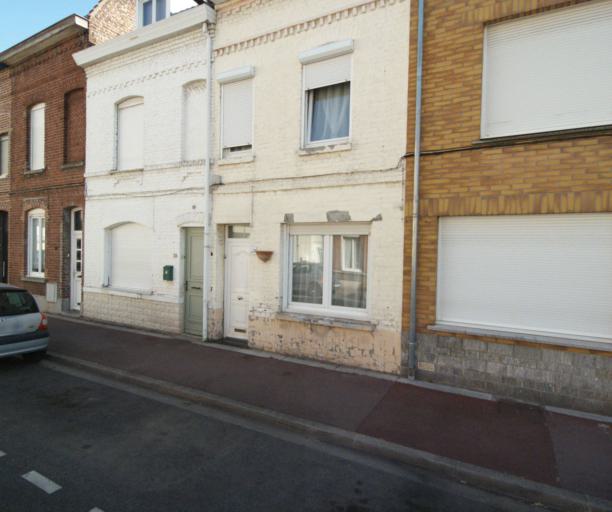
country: FR
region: Nord-Pas-de-Calais
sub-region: Departement du Nord
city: Tourcoing
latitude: 50.7105
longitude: 3.1616
